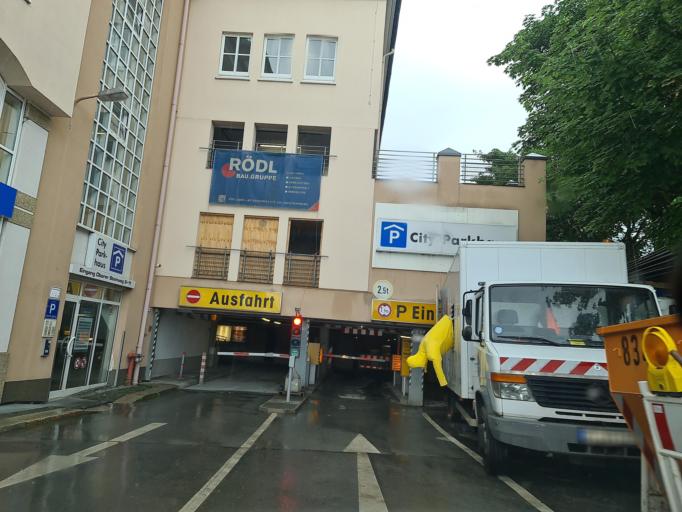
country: DE
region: Saxony
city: Plauen
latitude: 50.4949
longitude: 12.1380
